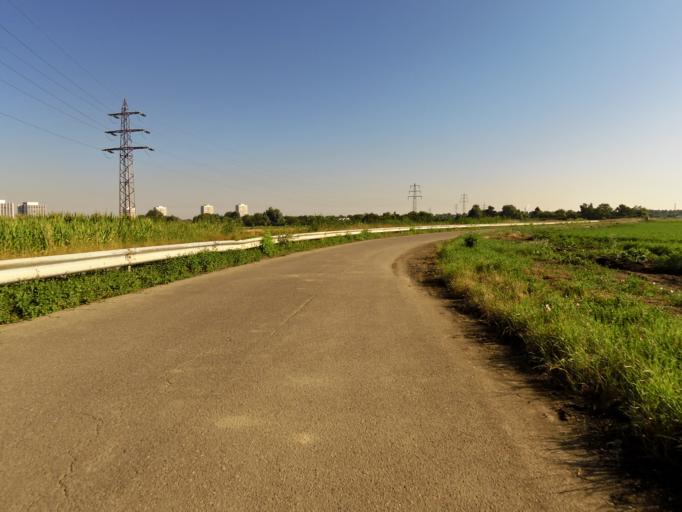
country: DE
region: Rheinland-Pfalz
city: Gartenstadt
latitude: 49.4793
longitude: 8.3960
